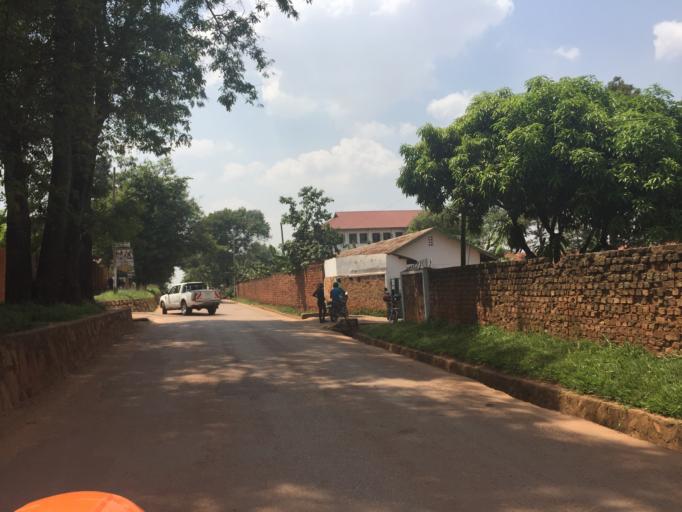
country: UG
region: Central Region
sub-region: Kampala District
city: Kampala
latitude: 0.3007
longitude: 32.5893
